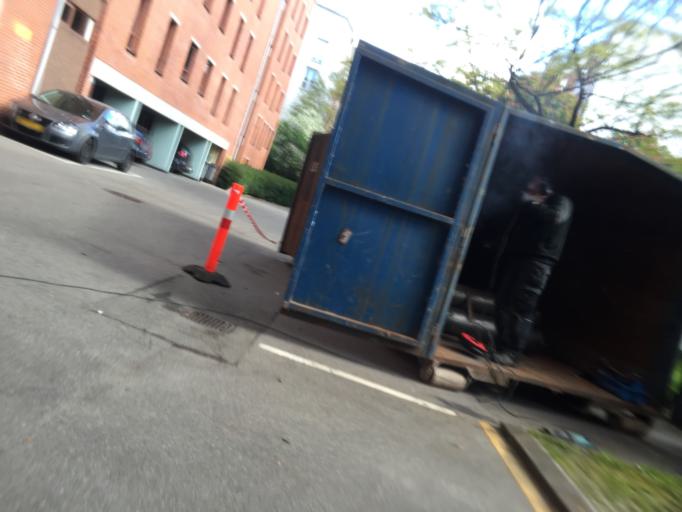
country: DK
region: Capital Region
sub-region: Frederiksberg Kommune
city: Frederiksberg
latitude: 55.6715
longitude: 12.5409
